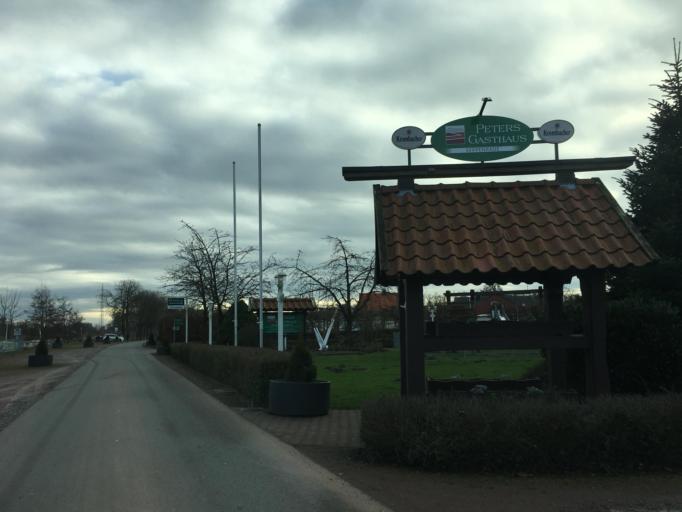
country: DE
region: North Rhine-Westphalia
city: Ludinghausen
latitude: 51.7779
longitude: 7.4093
